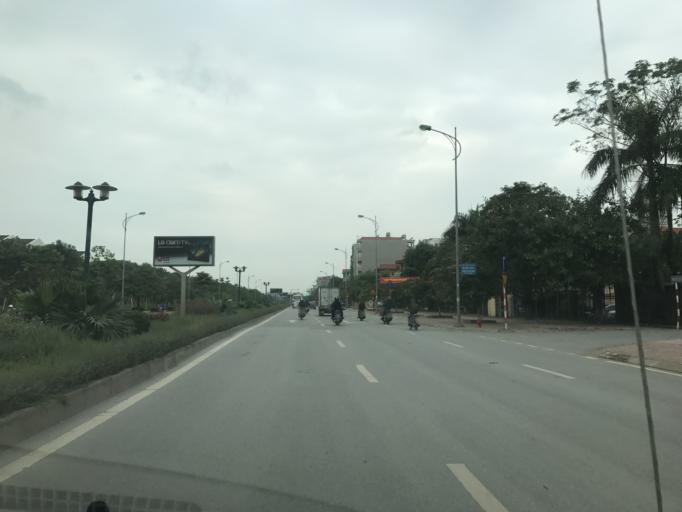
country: VN
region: Ha Noi
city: Ha Dong
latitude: 20.9643
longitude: 105.7617
